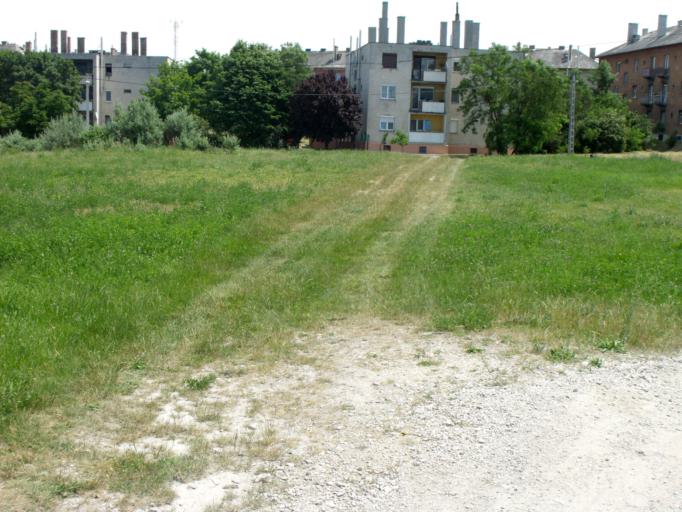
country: HU
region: Komarom-Esztergom
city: Labatlan
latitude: 47.7485
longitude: 18.4965
